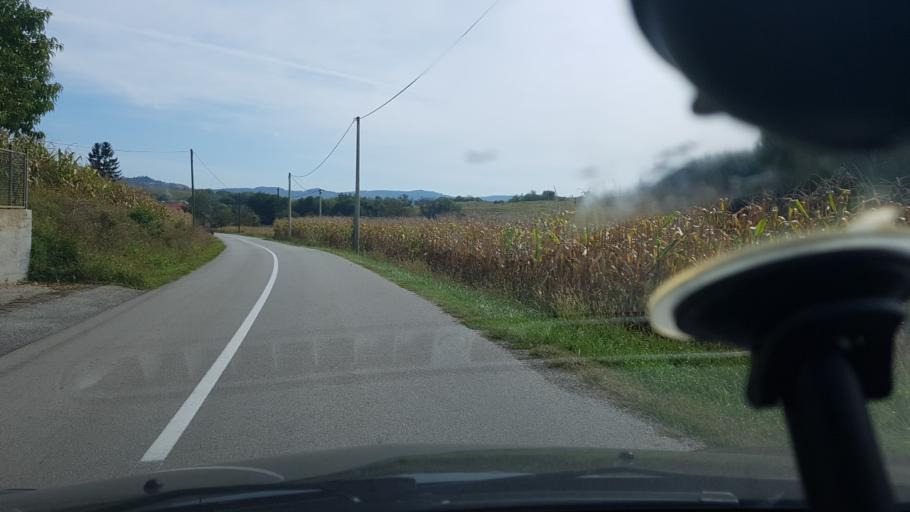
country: HR
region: Varazdinska
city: Remetinec
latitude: 46.1100
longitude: 16.2349
